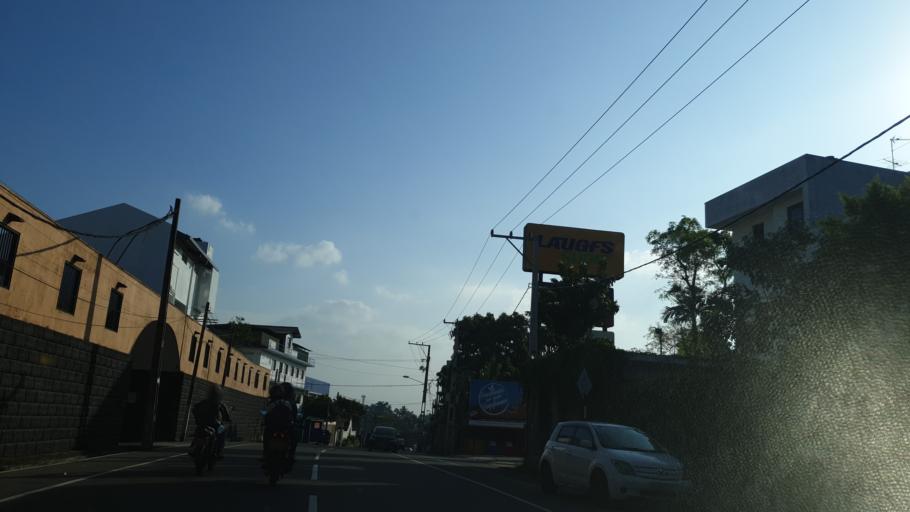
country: LK
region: Western
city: Sri Jayewardenepura Kotte
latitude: 6.8620
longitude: 79.8954
